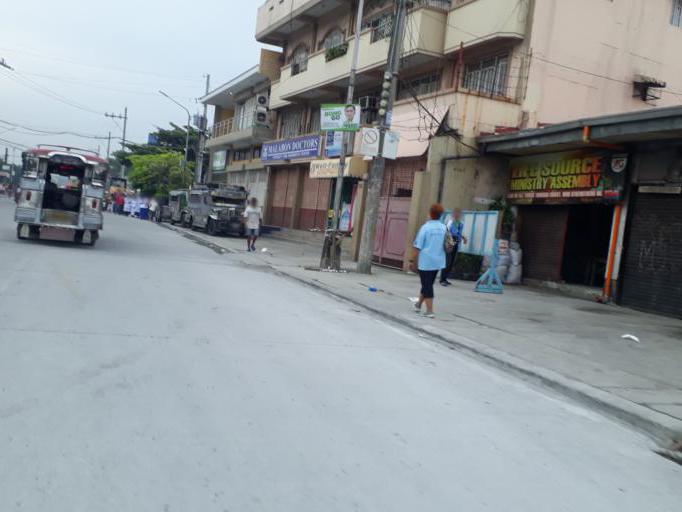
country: PH
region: Metro Manila
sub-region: Caloocan City
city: Niugan
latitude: 14.6598
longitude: 120.9592
